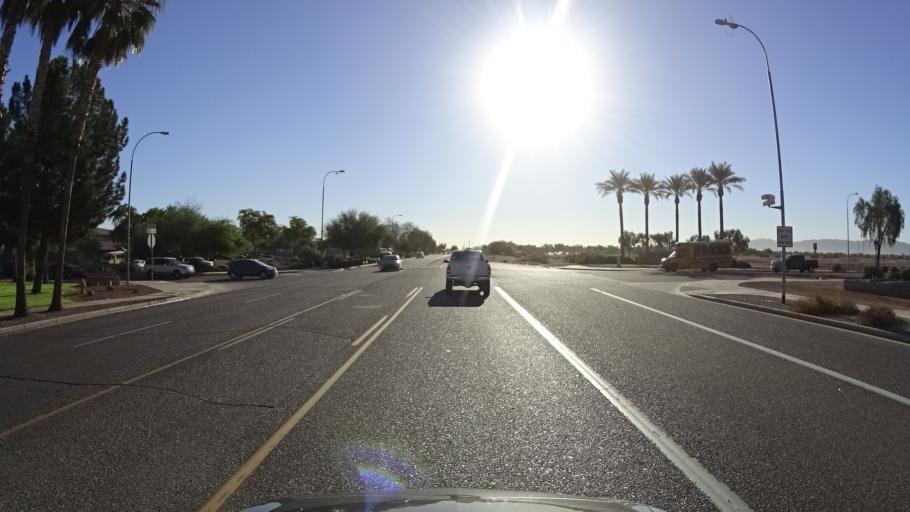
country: US
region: Arizona
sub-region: Maricopa County
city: Tolleson
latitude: 33.4230
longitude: -112.2304
